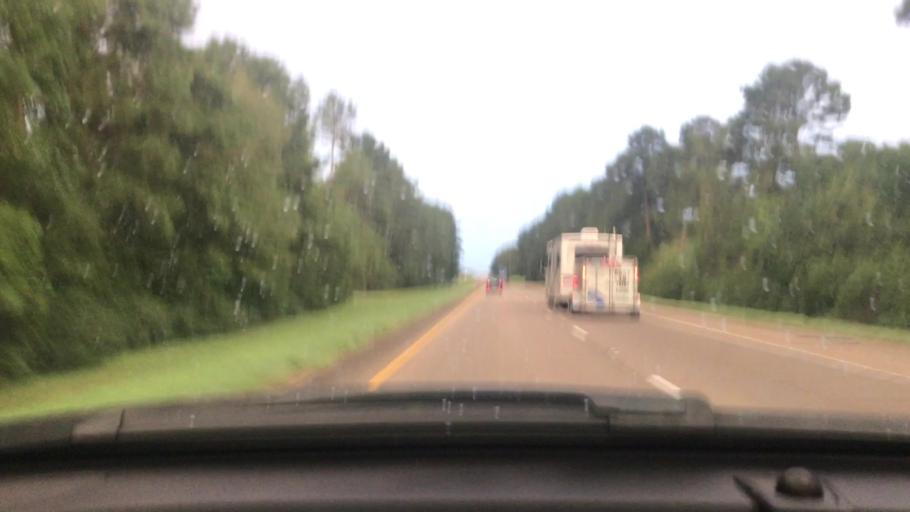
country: US
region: Louisiana
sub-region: Tangipahoa Parish
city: Roseland
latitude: 30.7933
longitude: -90.5333
